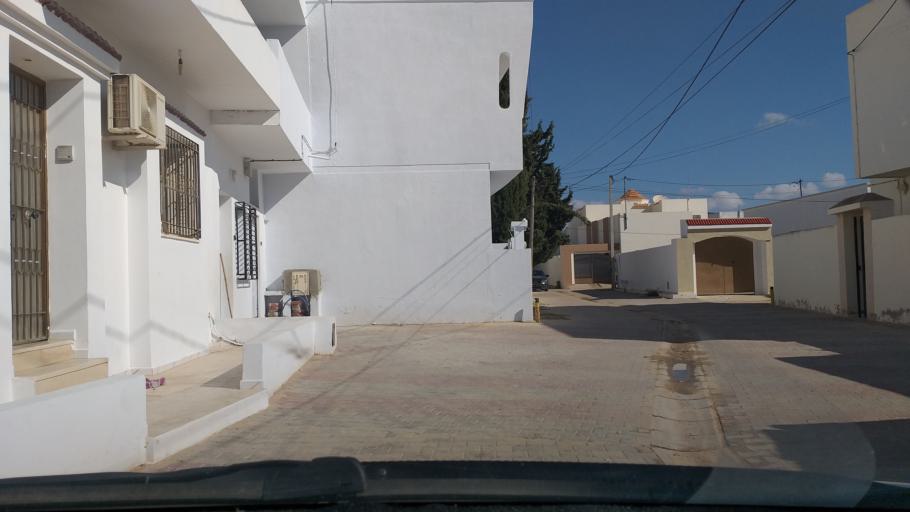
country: TN
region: Safaqis
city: Al Qarmadah
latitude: 34.8016
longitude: 10.7693
